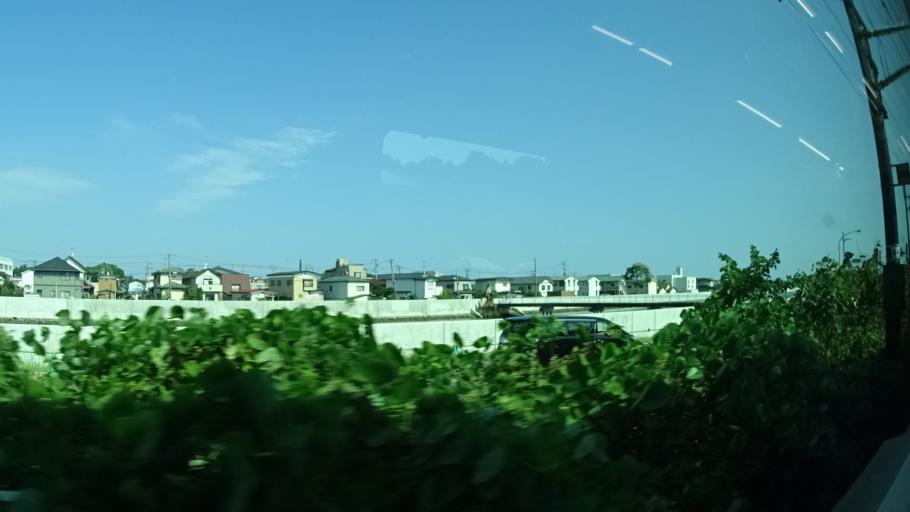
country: JP
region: Miyagi
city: Matsushima
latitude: 38.3848
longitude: 141.0675
